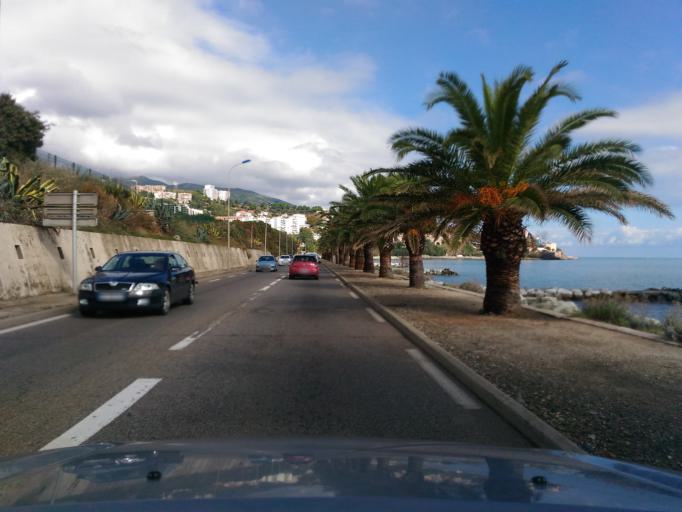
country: FR
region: Corsica
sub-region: Departement de la Haute-Corse
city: Bastia
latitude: 42.6816
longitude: 9.4467
